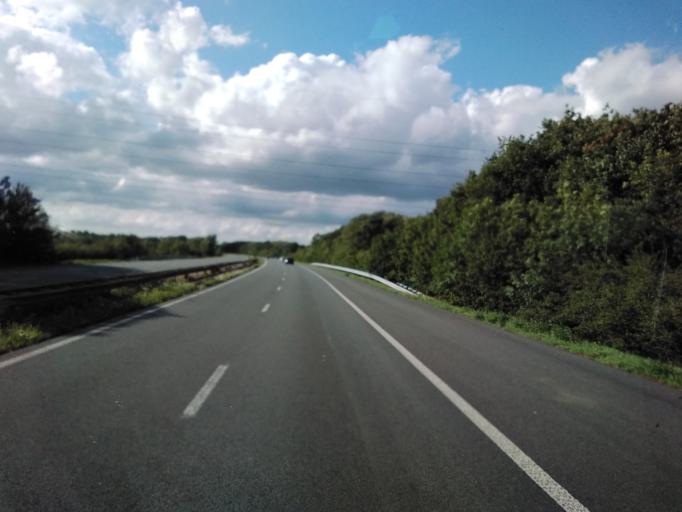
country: NL
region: Gelderland
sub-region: Gemeente Buren
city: Lienden
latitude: 51.9047
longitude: 5.4948
